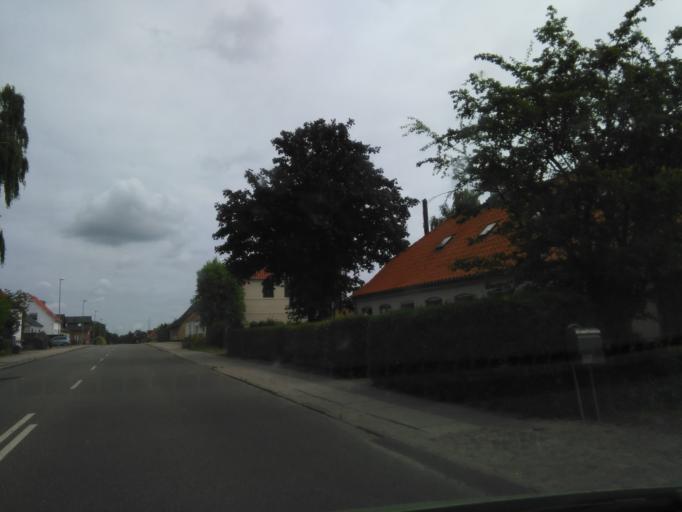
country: DK
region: Central Jutland
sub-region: Arhus Kommune
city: Beder
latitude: 56.0569
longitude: 10.2026
